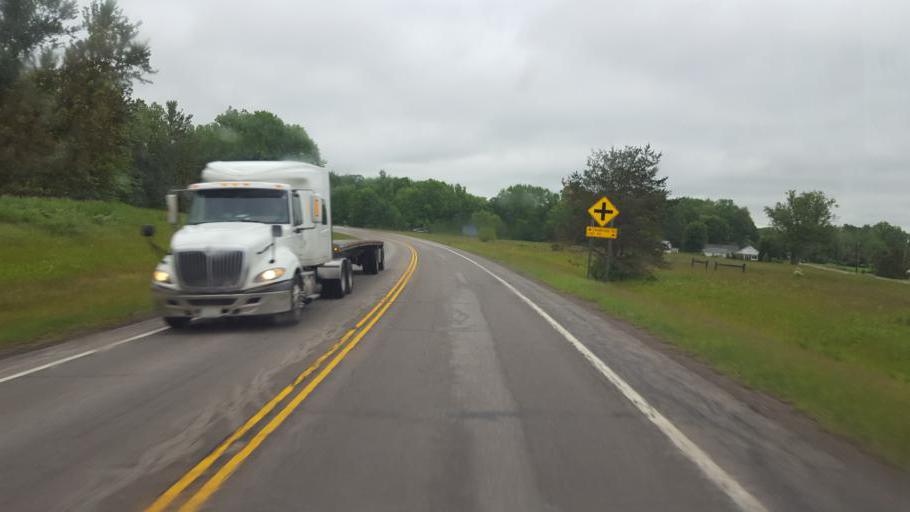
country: US
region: Ohio
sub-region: Medina County
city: Lodi
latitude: 41.0117
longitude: -82.0530
